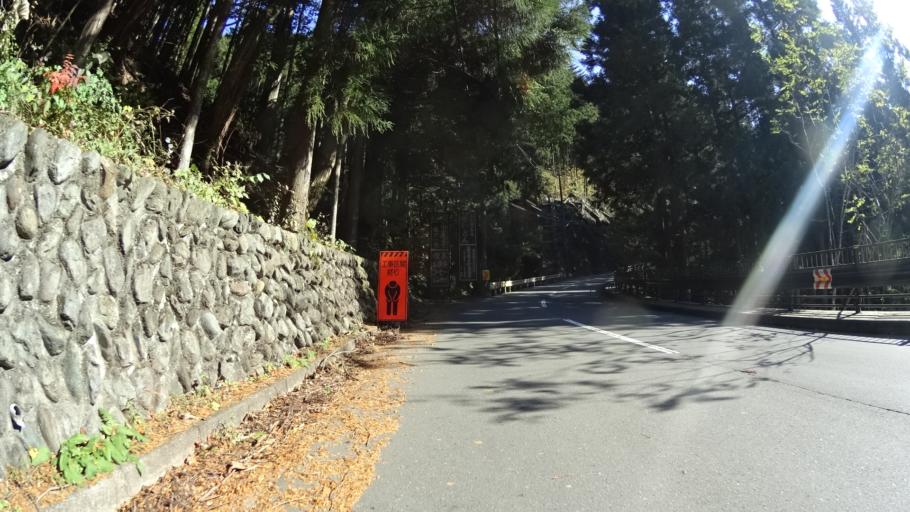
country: JP
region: Yamanashi
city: Uenohara
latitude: 35.7052
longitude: 139.1007
